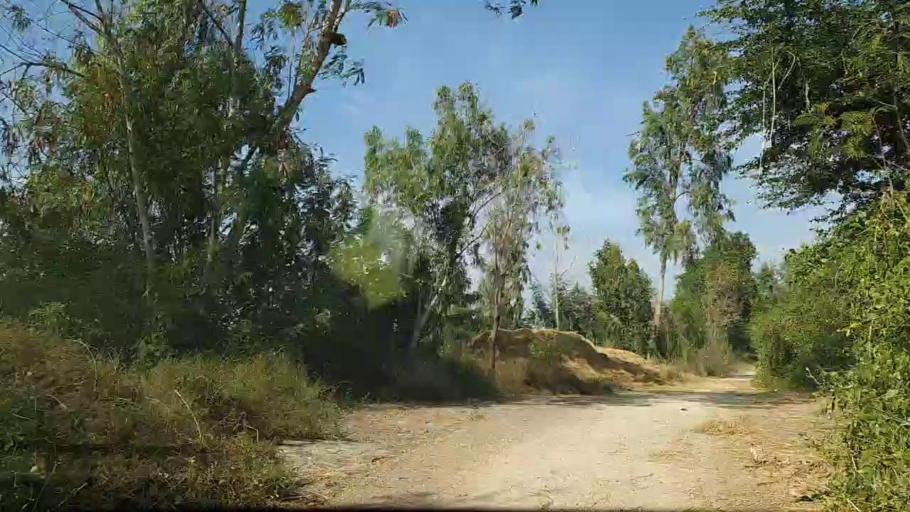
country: PK
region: Sindh
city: Daro Mehar
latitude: 24.7027
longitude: 68.1491
